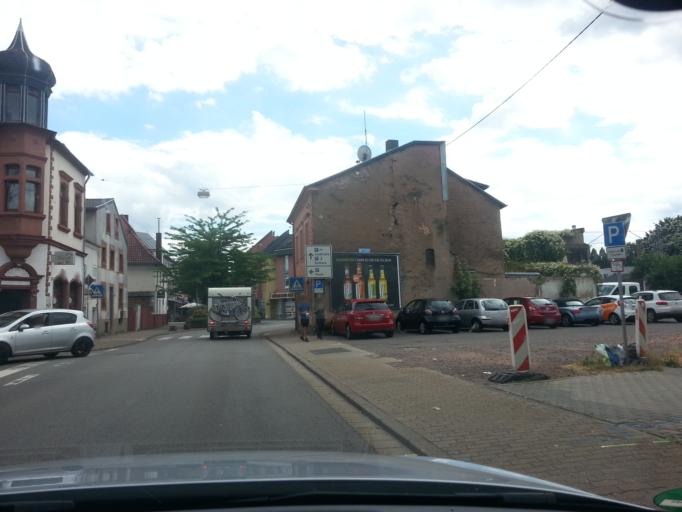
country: DE
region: Saarland
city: Merzig
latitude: 49.4460
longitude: 6.6365
